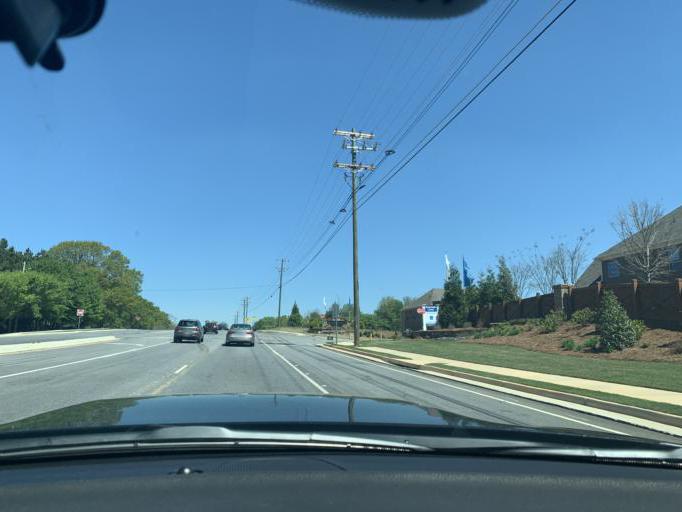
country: US
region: Georgia
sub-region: Forsyth County
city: Cumming
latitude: 34.1905
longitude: -84.1968
